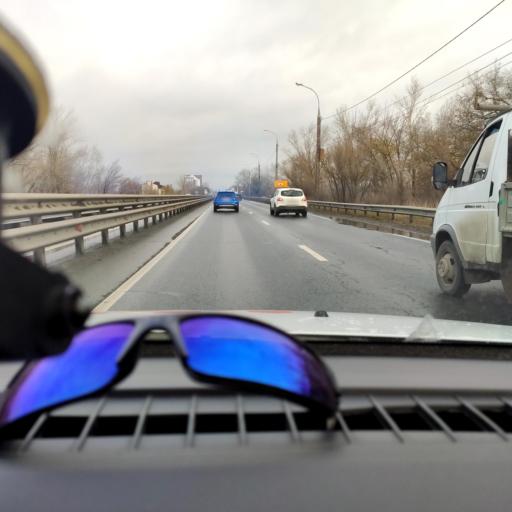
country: RU
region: Samara
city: Samara
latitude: 53.1055
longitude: 50.1631
